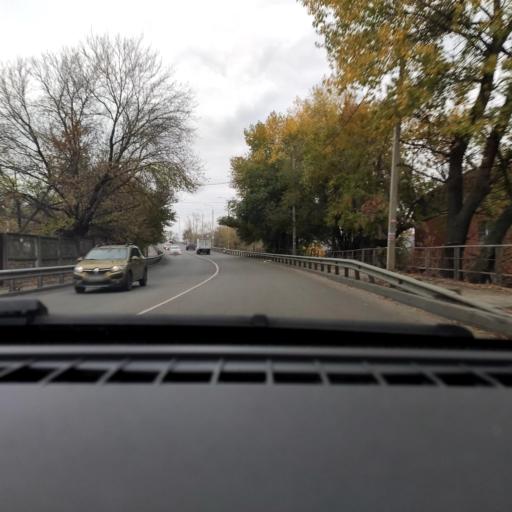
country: RU
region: Voronezj
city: Voronezh
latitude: 51.7290
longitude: 39.2599
